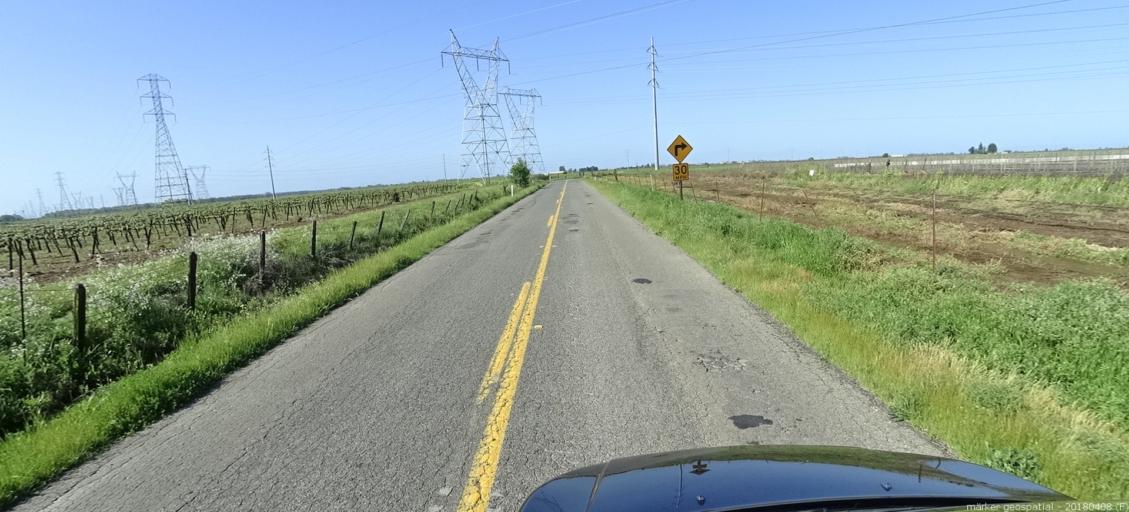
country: US
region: California
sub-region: Sacramento County
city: Elk Grove
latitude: 38.3625
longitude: -121.3515
